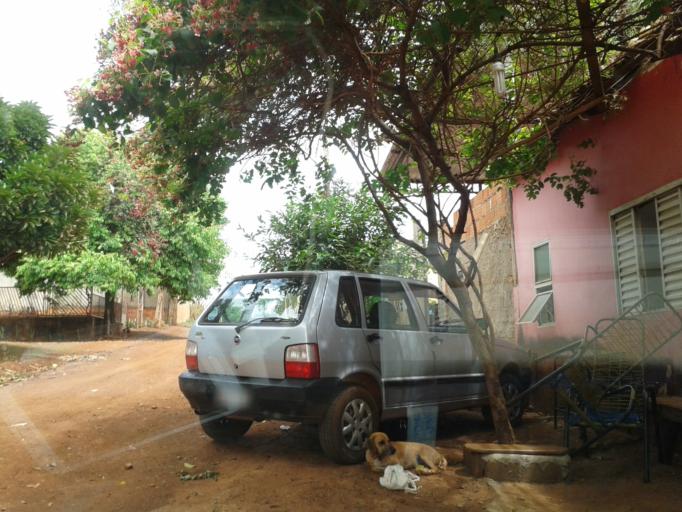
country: BR
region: Goias
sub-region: Itumbiara
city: Itumbiara
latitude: -18.4257
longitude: -49.1907
